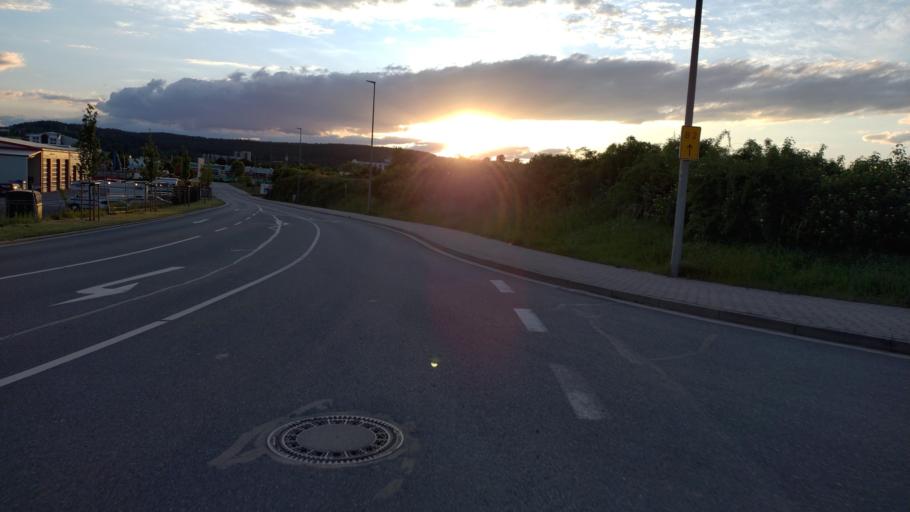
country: DE
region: Bavaria
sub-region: Upper Franconia
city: Bindlach
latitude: 49.9695
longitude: 11.6171
